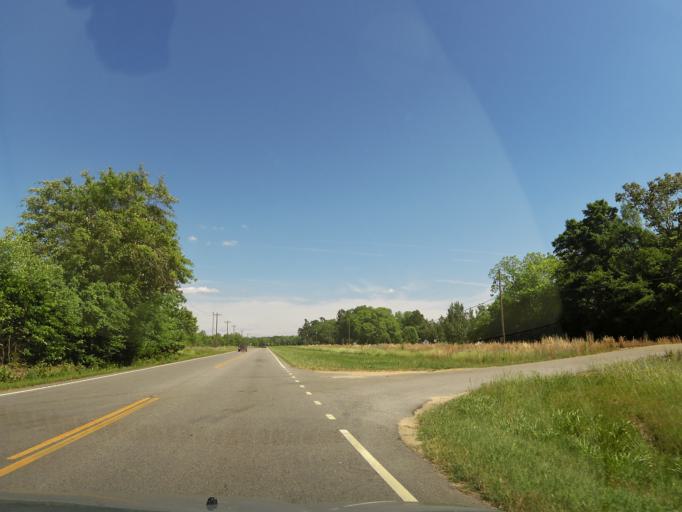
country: US
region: South Carolina
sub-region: Aiken County
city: Aiken
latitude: 33.5326
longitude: -81.6438
